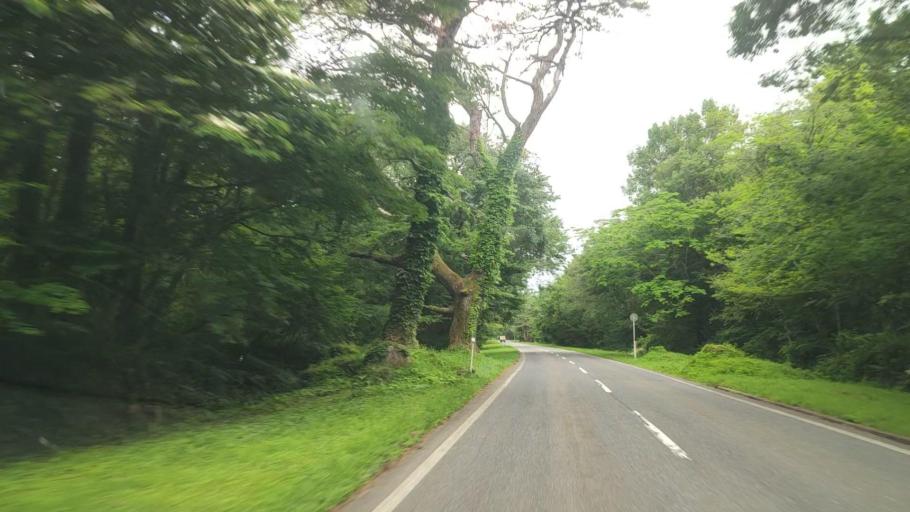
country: JP
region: Tottori
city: Yonago
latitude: 35.3991
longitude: 133.5042
